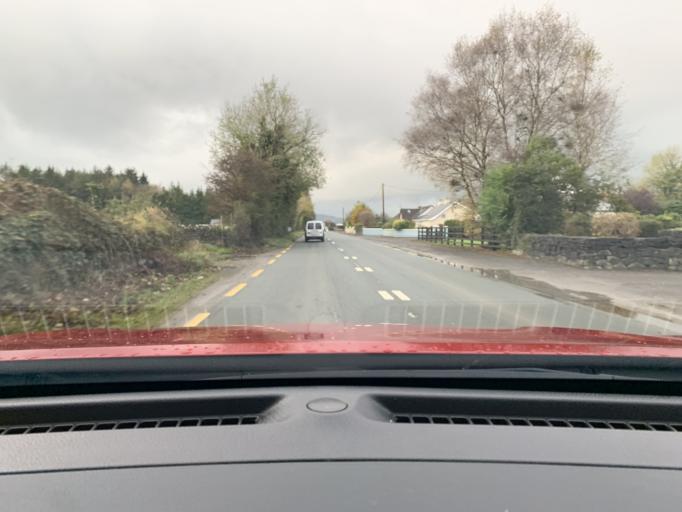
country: IE
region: Connaught
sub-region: Sligo
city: Collooney
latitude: 54.1979
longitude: -8.4967
